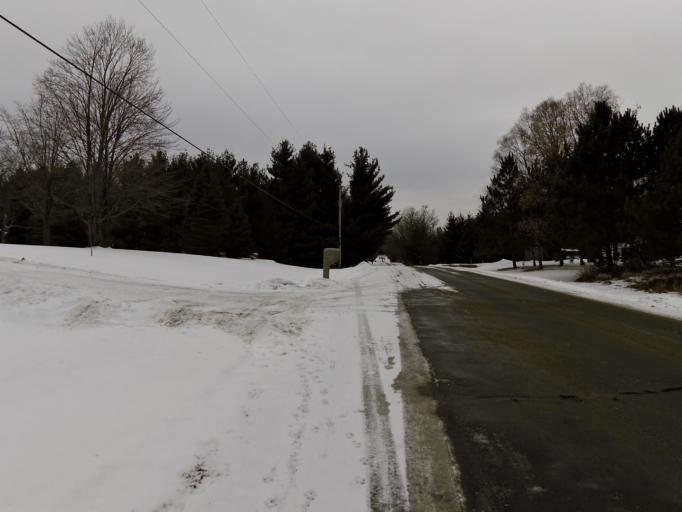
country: US
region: Minnesota
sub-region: Washington County
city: Lake Elmo
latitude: 44.9575
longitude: -92.8364
